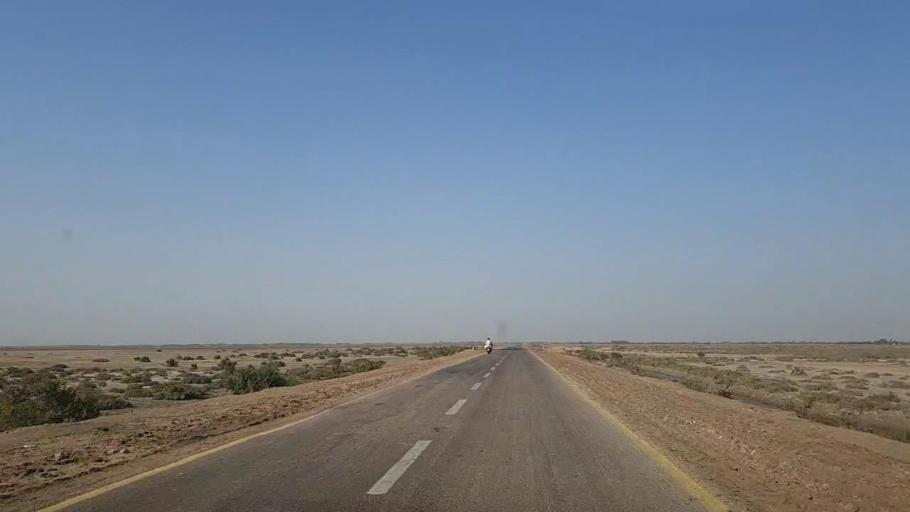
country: PK
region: Sindh
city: Jati
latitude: 24.4900
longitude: 68.3751
